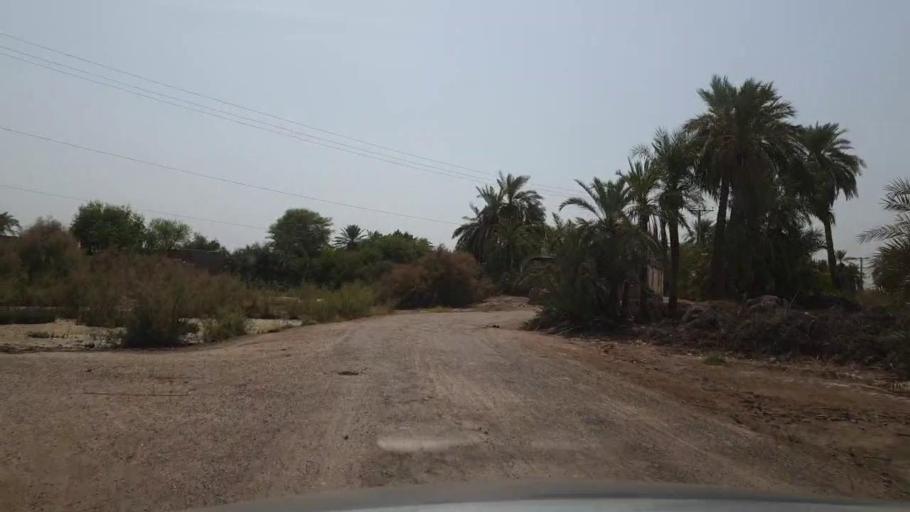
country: PK
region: Sindh
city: Garhi Yasin
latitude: 27.8901
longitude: 68.4658
